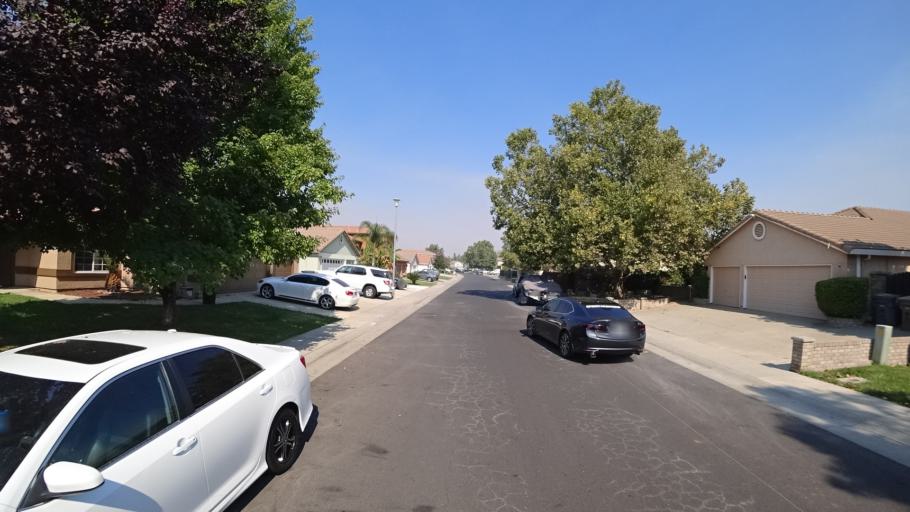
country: US
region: California
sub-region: Sacramento County
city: Laguna
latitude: 38.4270
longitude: -121.4137
